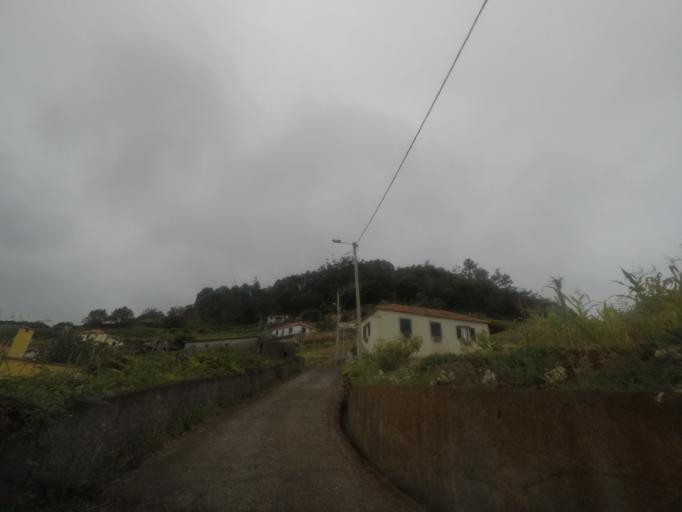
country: PT
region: Madeira
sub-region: Santana
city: Santana
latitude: 32.7684
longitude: -16.8491
